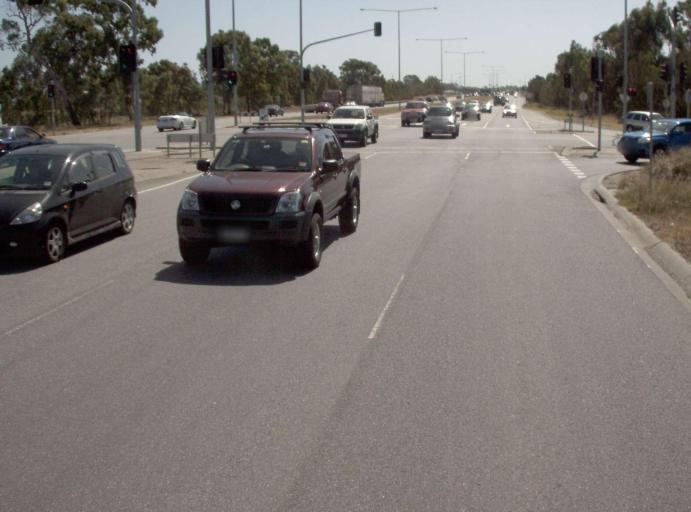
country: AU
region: Victoria
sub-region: Greater Dandenong
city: Keysborough
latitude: -37.9998
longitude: 145.1814
